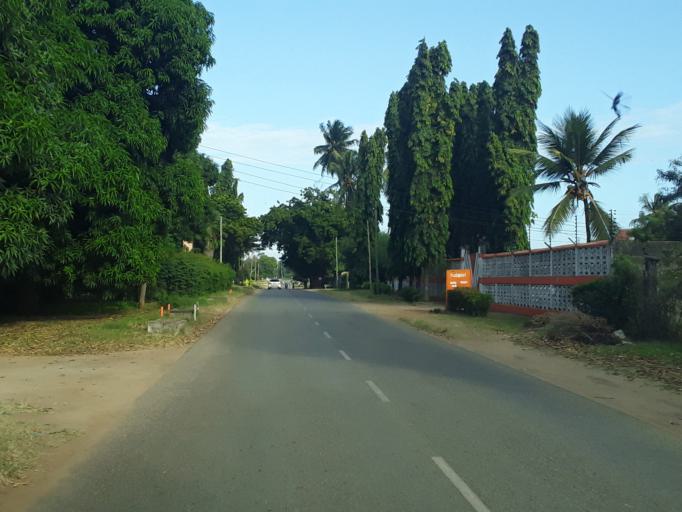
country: TZ
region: Tanga
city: Tanga
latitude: -5.0728
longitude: 39.1125
